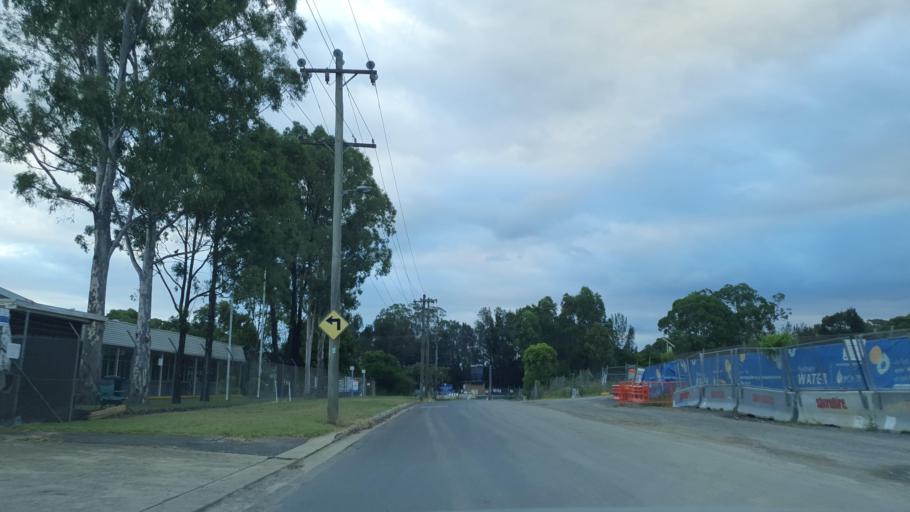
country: AU
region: New South Wales
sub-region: Penrith Municipality
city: Werrington County
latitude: -33.7397
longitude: 150.7627
